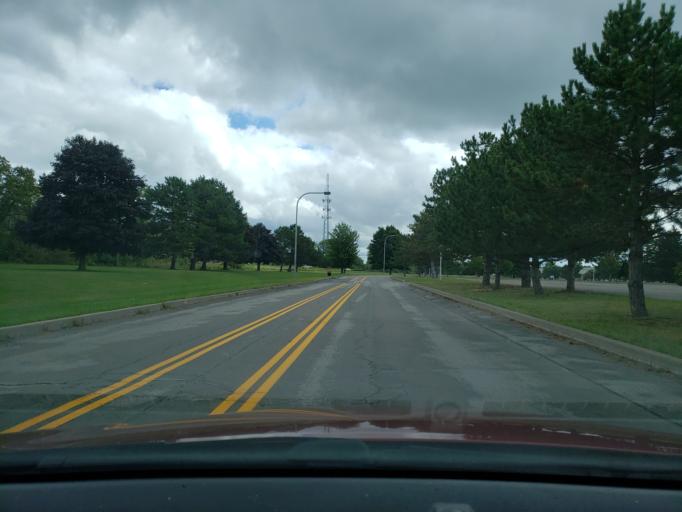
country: US
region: New York
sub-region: Monroe County
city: North Gates
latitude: 43.1566
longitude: -77.7360
